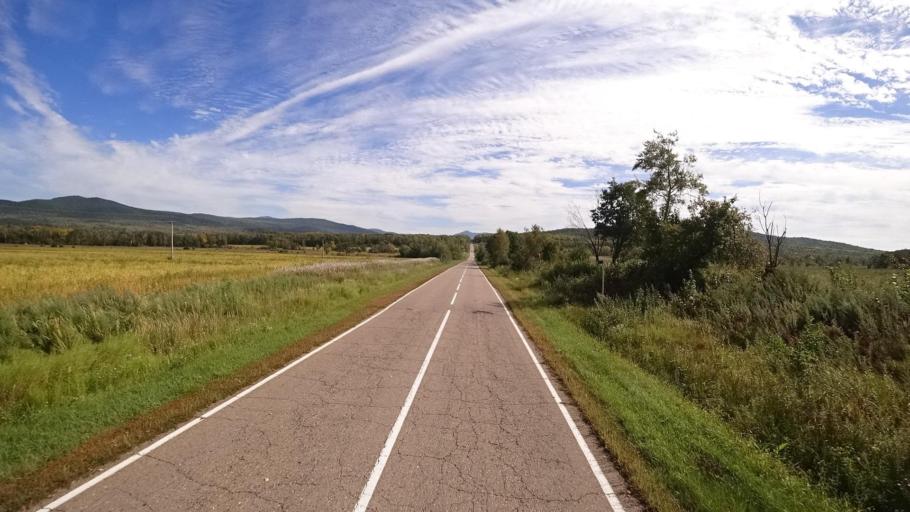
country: RU
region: Primorskiy
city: Yakovlevka
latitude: 44.4126
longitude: 133.5866
